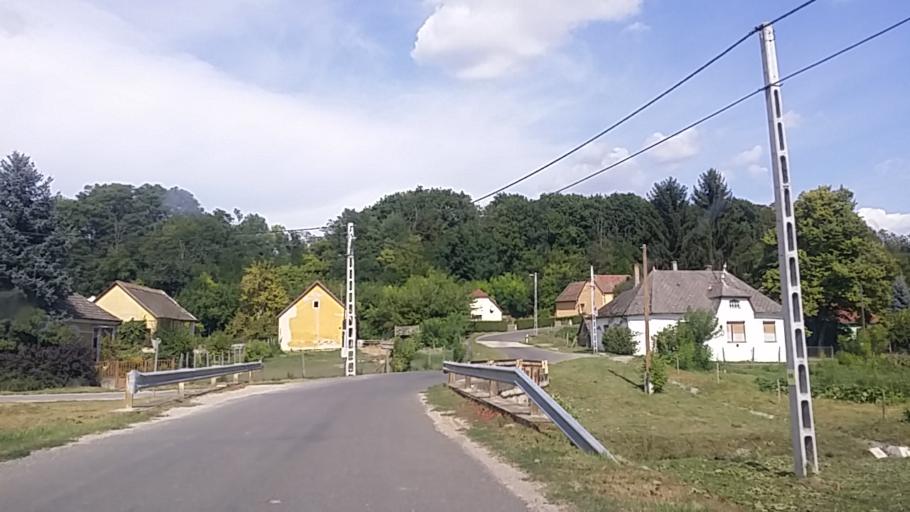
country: HU
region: Tolna
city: Gyonk
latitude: 46.5380
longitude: 18.4733
